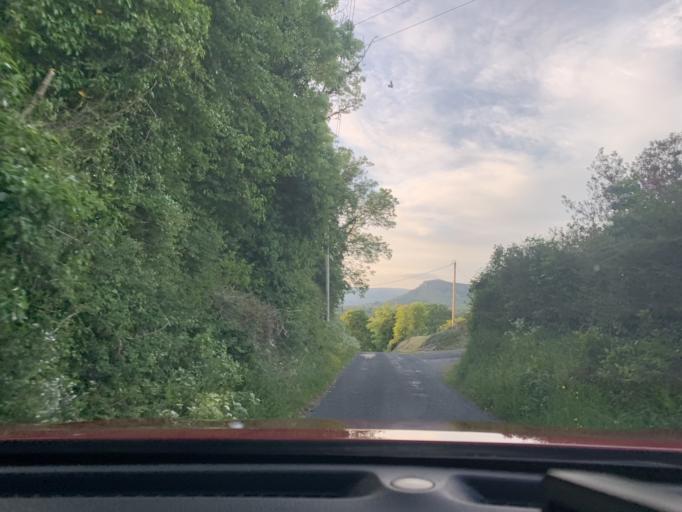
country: IE
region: Connaught
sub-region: Sligo
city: Sligo
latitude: 54.2879
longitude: -8.4309
